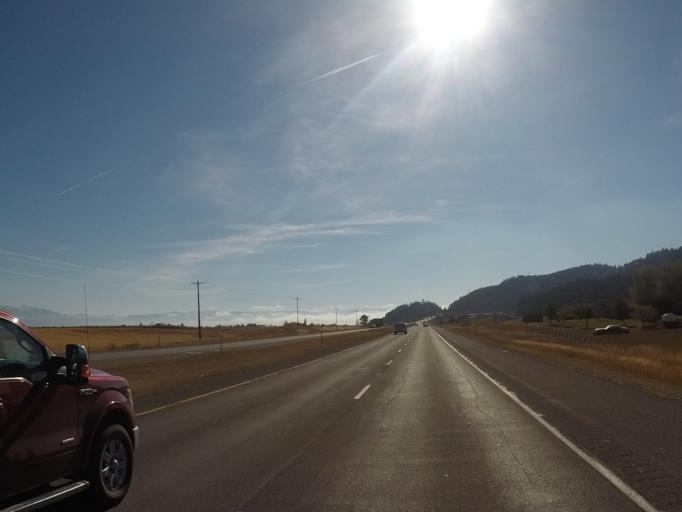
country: US
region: Montana
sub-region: Flathead County
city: Somers
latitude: 48.1039
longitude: -114.2445
